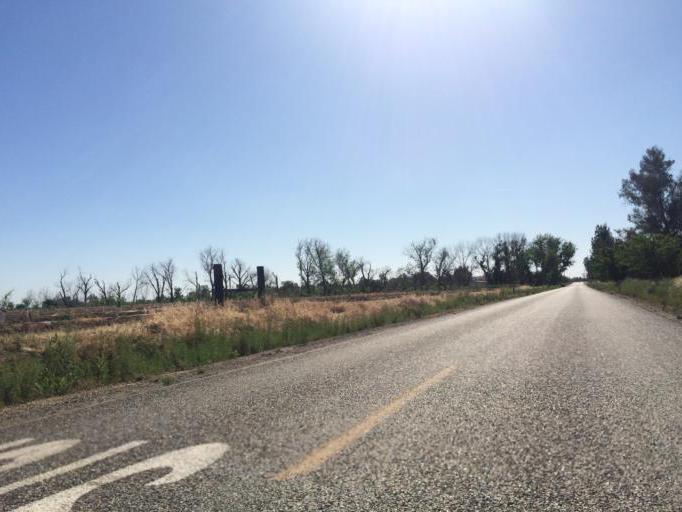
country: US
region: California
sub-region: Fresno County
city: Tarpey Village
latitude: 36.7867
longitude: -119.6123
